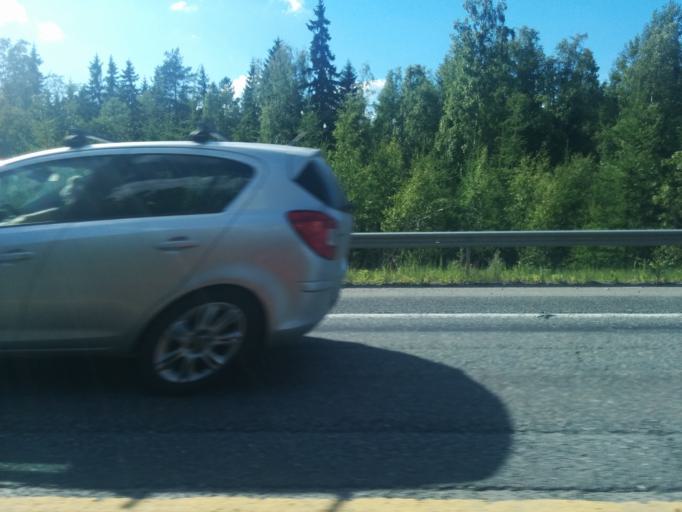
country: FI
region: Pirkanmaa
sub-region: Tampere
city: Tampere
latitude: 61.5169
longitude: 23.9171
